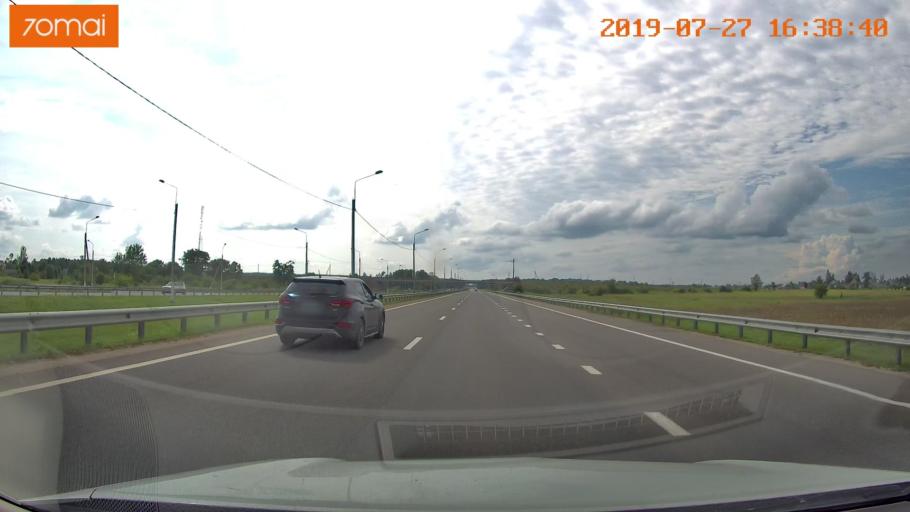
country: RU
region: Kaliningrad
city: Gvardeysk
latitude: 54.6490
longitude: 21.2219
